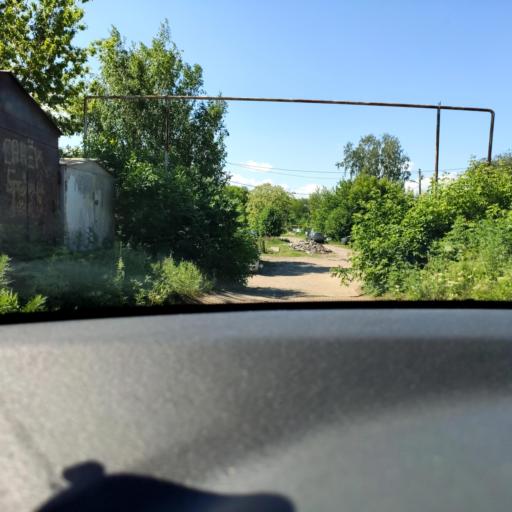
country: RU
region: Samara
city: Samara
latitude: 53.2131
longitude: 50.2634
